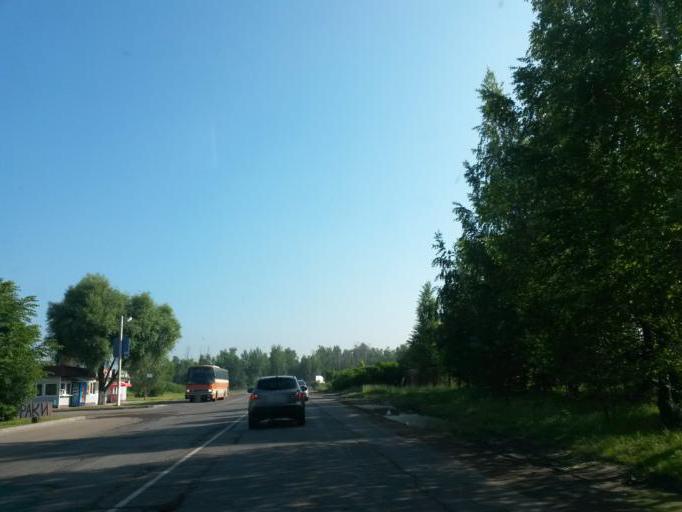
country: RU
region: Moskovskaya
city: Gorki-Leninskiye
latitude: 55.5080
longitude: 37.7826
